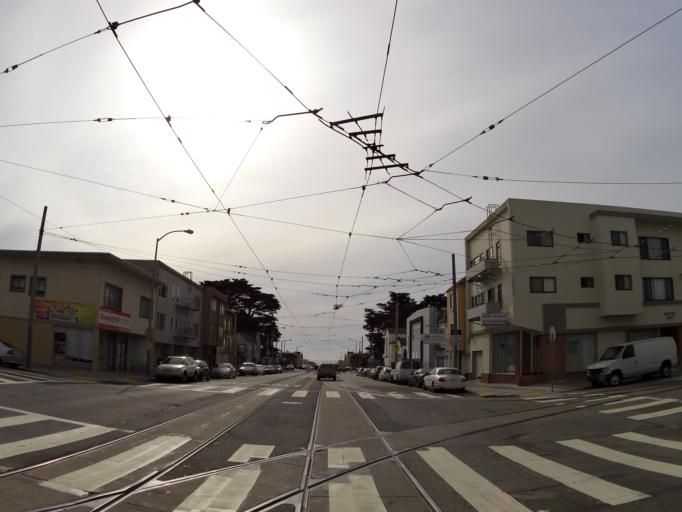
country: US
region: California
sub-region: San Mateo County
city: Daly City
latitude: 37.7423
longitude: -122.4927
